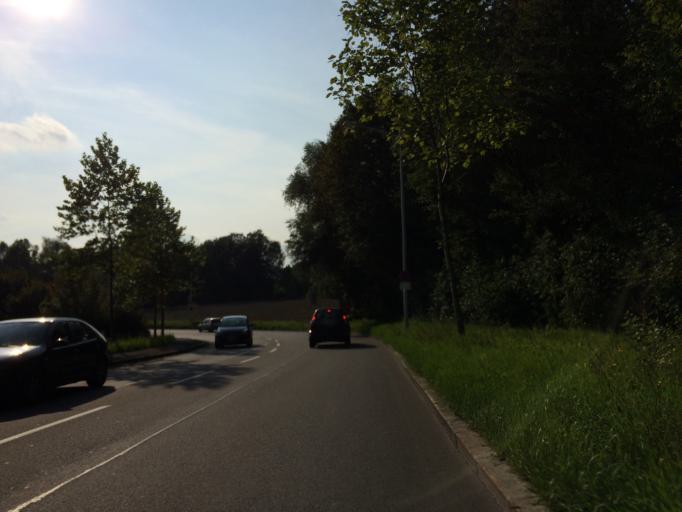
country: AT
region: Upper Austria
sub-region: Linz Stadt
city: Linz
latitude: 48.2932
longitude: 14.2718
